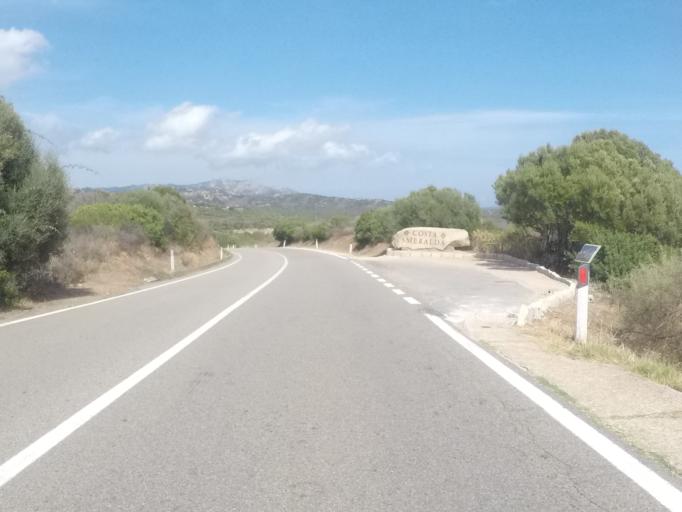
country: IT
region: Sardinia
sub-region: Provincia di Olbia-Tempio
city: Porto Cervo
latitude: 41.0446
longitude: 9.5187
